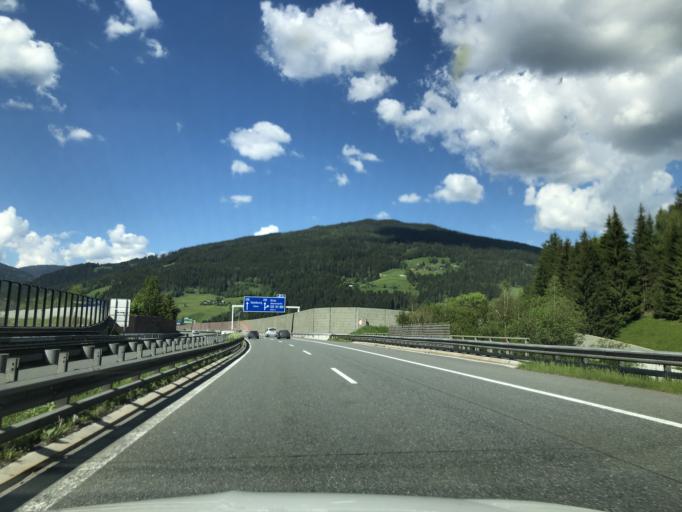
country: AT
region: Salzburg
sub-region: Politischer Bezirk Sankt Johann im Pongau
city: Altenmarkt im Pongau
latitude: 47.3787
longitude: 13.4004
